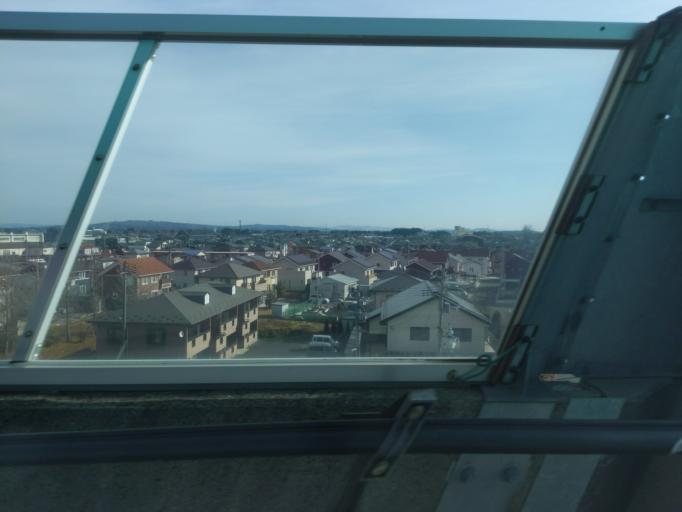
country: JP
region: Miyagi
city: Furukawa
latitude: 38.5793
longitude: 140.9700
